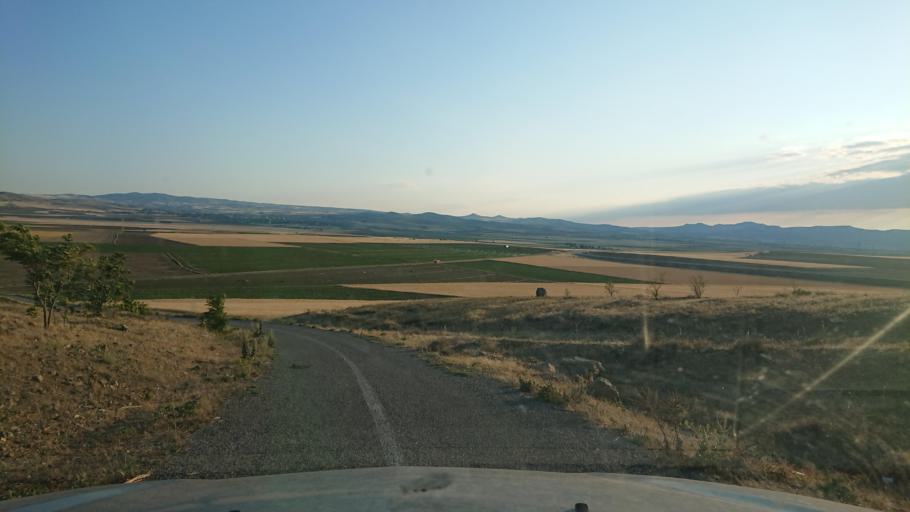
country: TR
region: Aksaray
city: Sariyahsi
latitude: 39.0220
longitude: 33.8893
